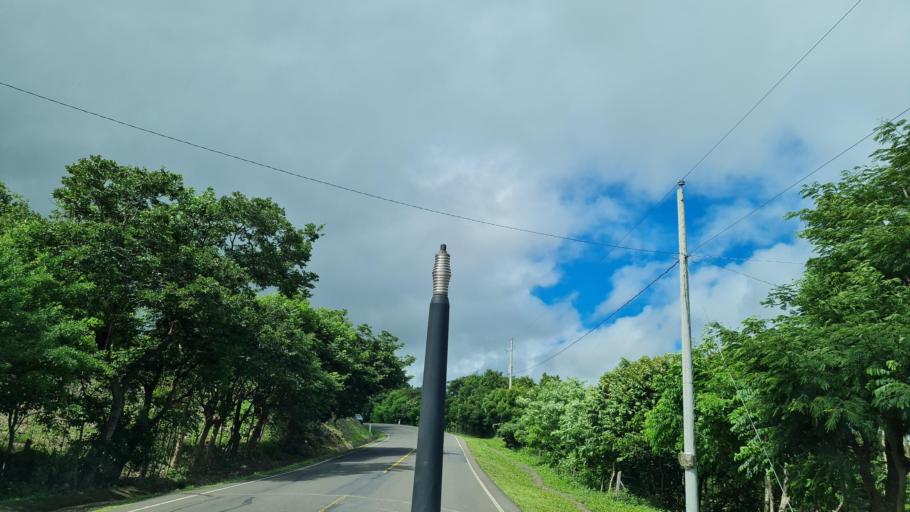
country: NI
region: Boaco
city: San Jose de los Remates
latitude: 12.6082
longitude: -85.8974
